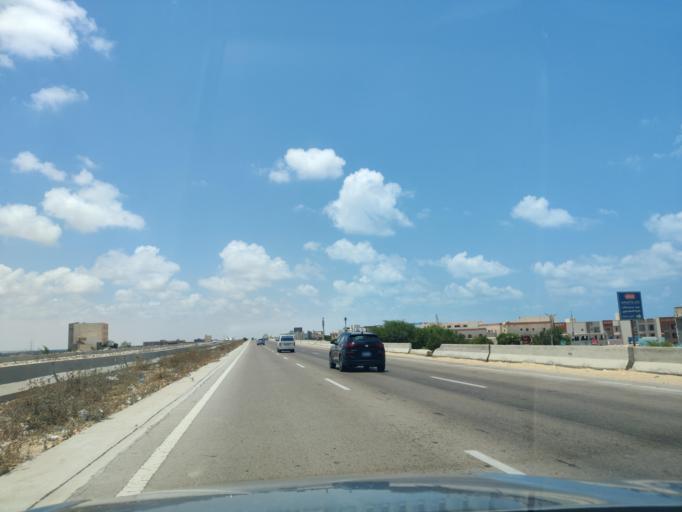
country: EG
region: Muhafazat Matruh
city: Al `Alamayn
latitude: 30.8397
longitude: 29.2524
